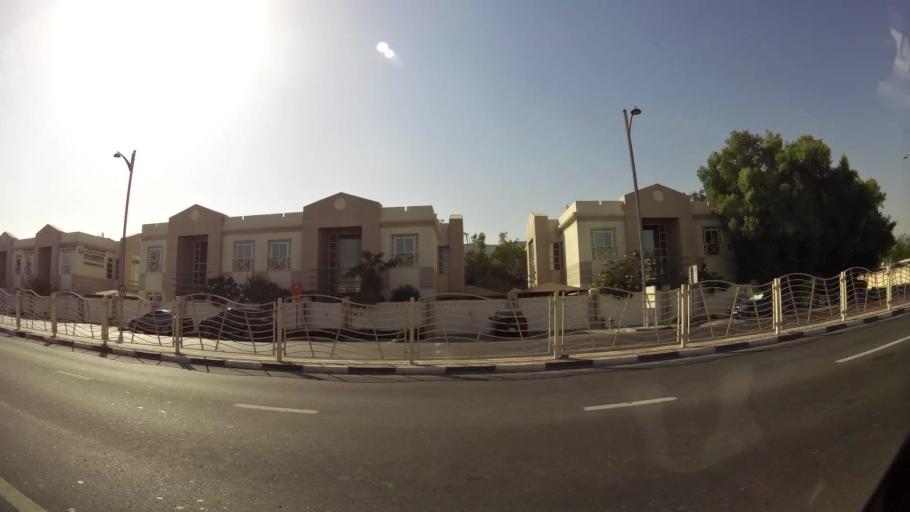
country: AE
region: Dubai
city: Dubai
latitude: 25.2244
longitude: 55.2576
